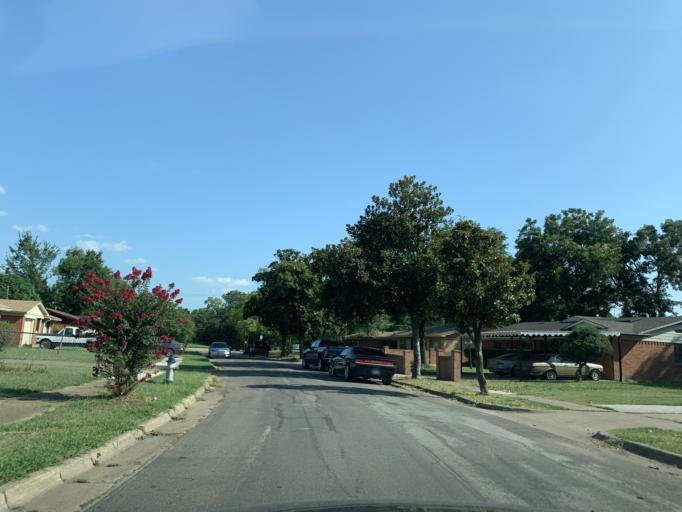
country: US
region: Texas
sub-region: Dallas County
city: Hutchins
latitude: 32.6892
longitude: -96.7855
